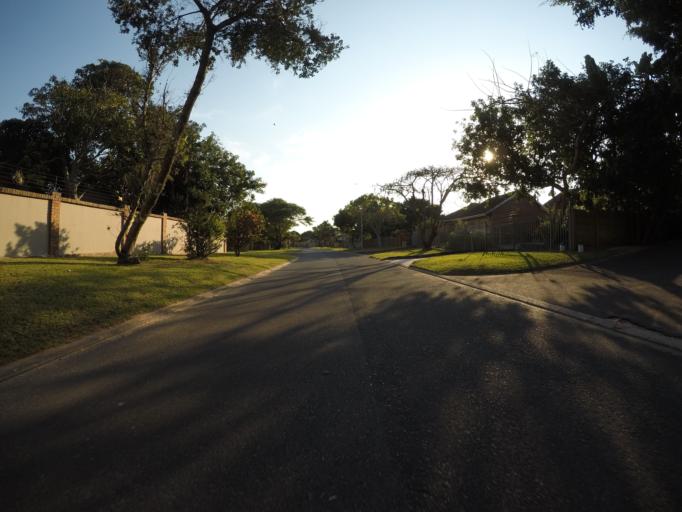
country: ZA
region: KwaZulu-Natal
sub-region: uThungulu District Municipality
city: Richards Bay
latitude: -28.7771
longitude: 32.1166
